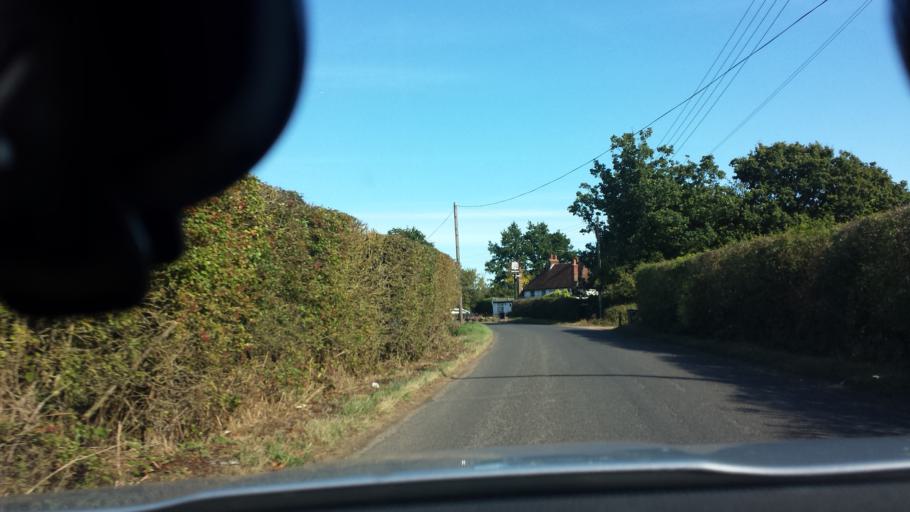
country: GB
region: England
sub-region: Kent
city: Staplehurst
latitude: 51.1948
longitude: 0.5532
